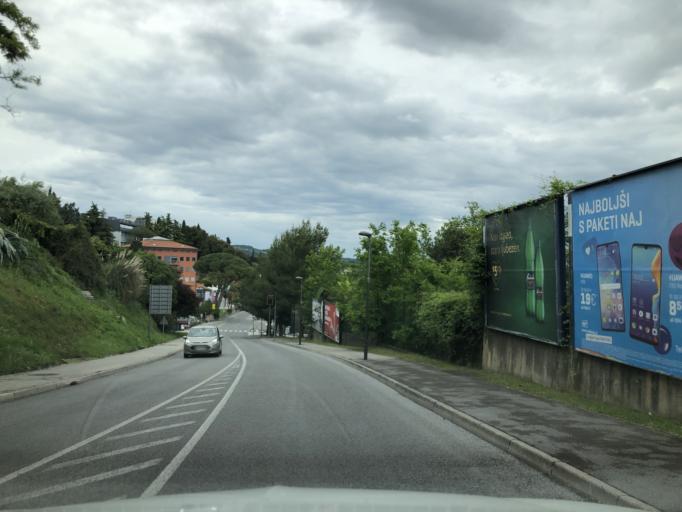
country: SI
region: Piran-Pirano
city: Piran
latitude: 45.5170
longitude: 13.5759
